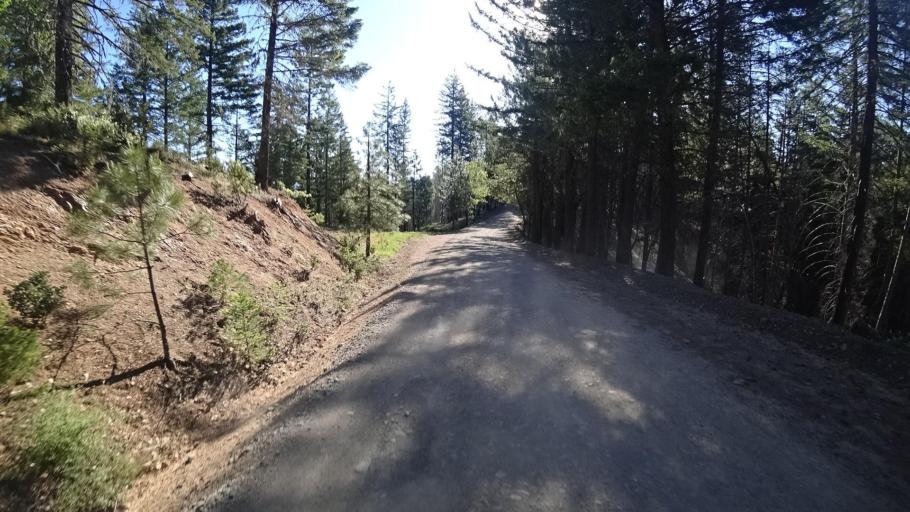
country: US
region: California
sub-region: Lake County
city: Upper Lake
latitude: 39.3579
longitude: -122.9865
